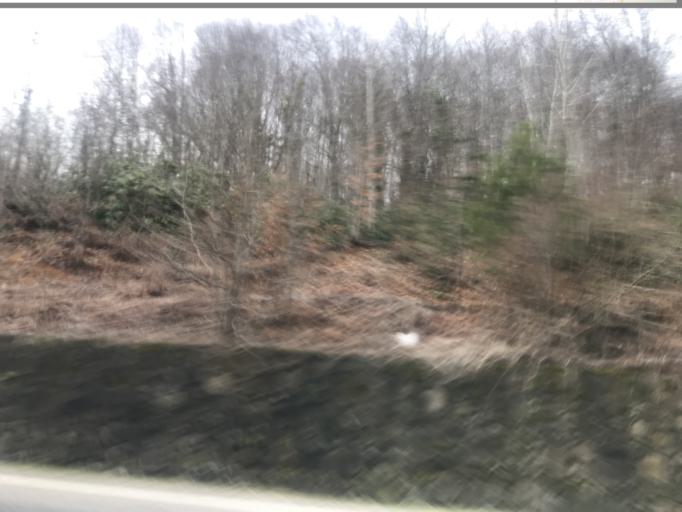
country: TR
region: Bartin
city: Amasra
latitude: 41.7136
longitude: 32.3925
